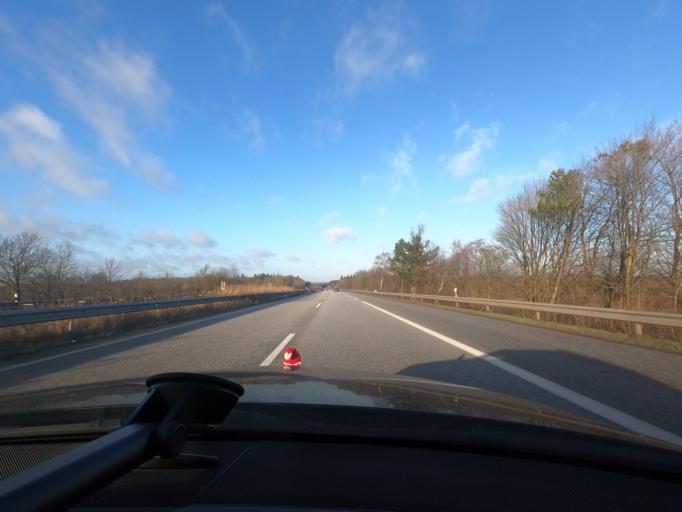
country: DE
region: Schleswig-Holstein
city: Tarp
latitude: 54.6662
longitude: 9.4295
